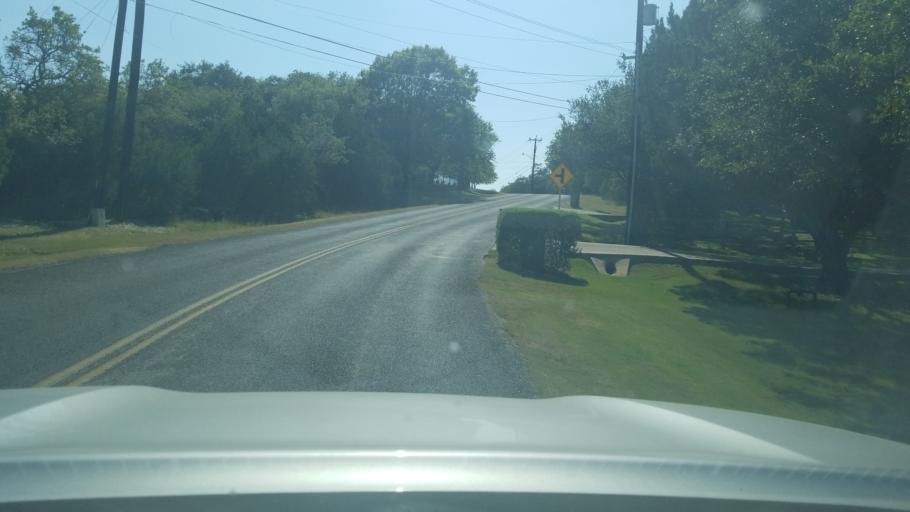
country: US
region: Texas
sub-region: Bexar County
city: Timberwood Park
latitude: 29.6813
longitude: -98.5025
